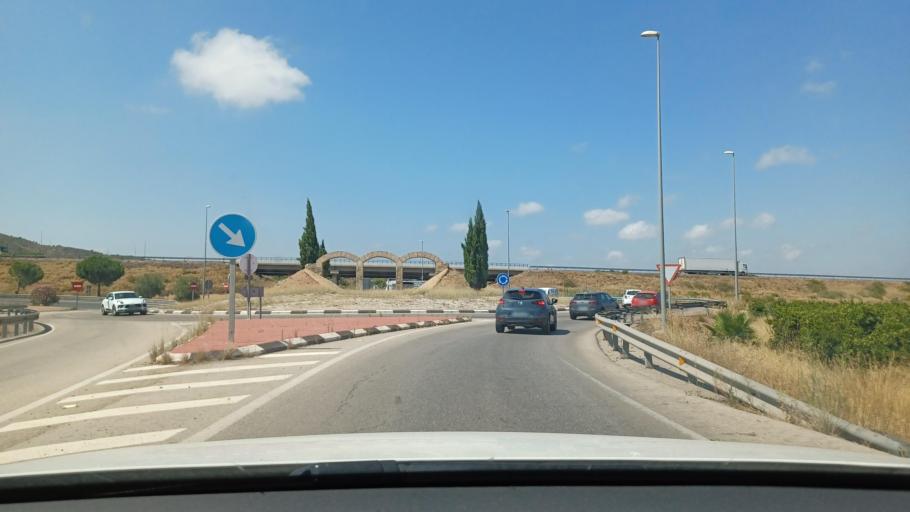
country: ES
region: Valencia
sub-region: Provincia de Valencia
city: Sagunto
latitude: 39.7002
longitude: -0.2613
